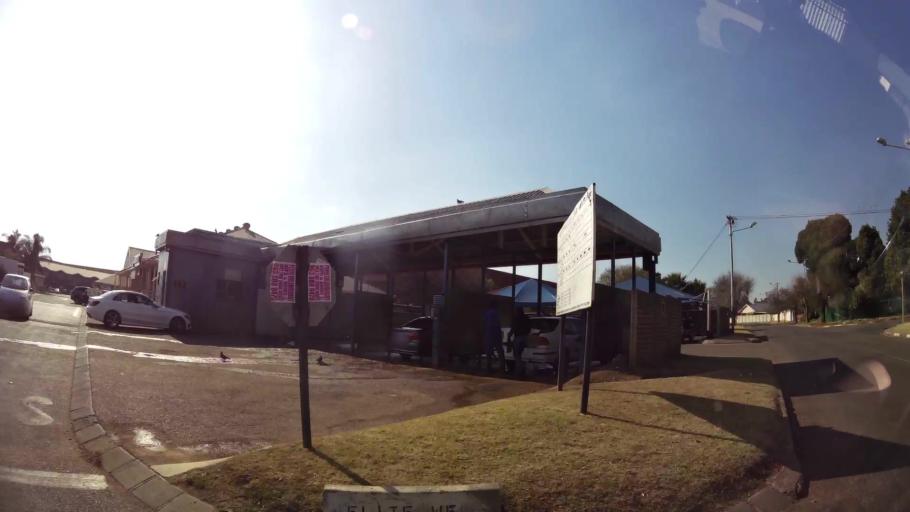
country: ZA
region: Gauteng
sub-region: West Rand District Municipality
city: Randfontein
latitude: -26.1676
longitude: 27.6987
